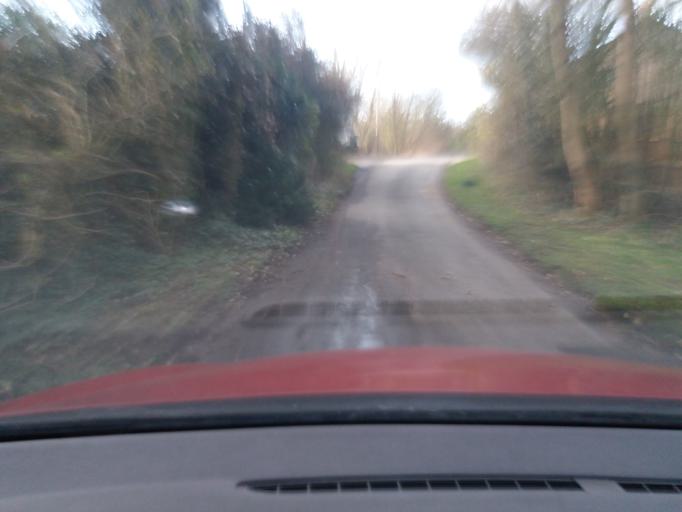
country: GB
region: England
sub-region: Lancashire
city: Euxton
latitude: 53.6504
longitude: -2.6681
